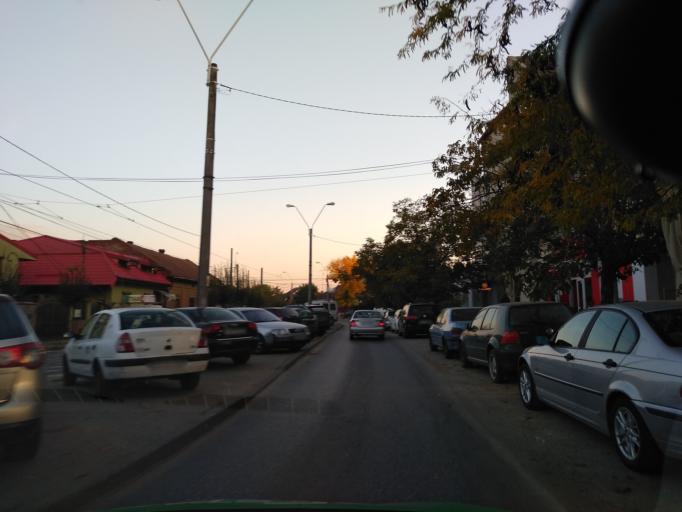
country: RO
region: Timis
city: Timisoara
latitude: 45.7314
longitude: 21.2279
